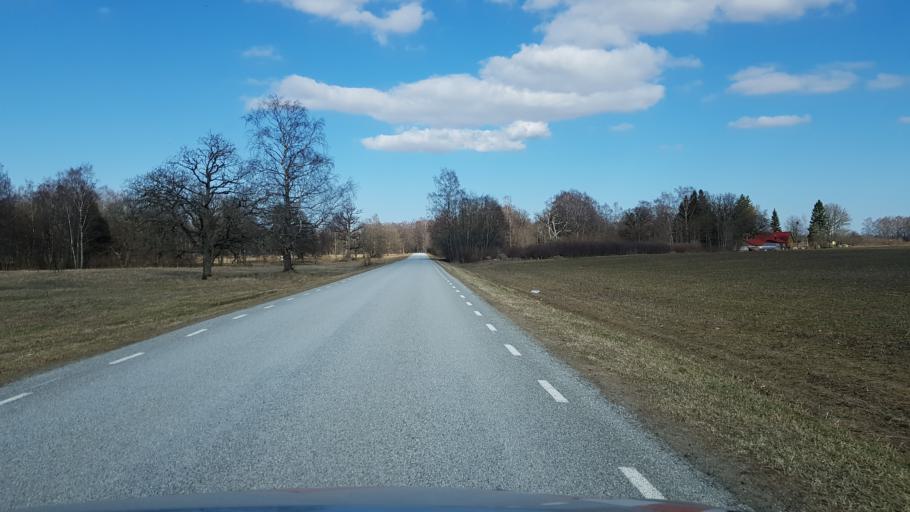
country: EE
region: Laeaene-Virumaa
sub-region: Rakvere linn
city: Rakvere
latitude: 59.3189
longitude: 26.2598
